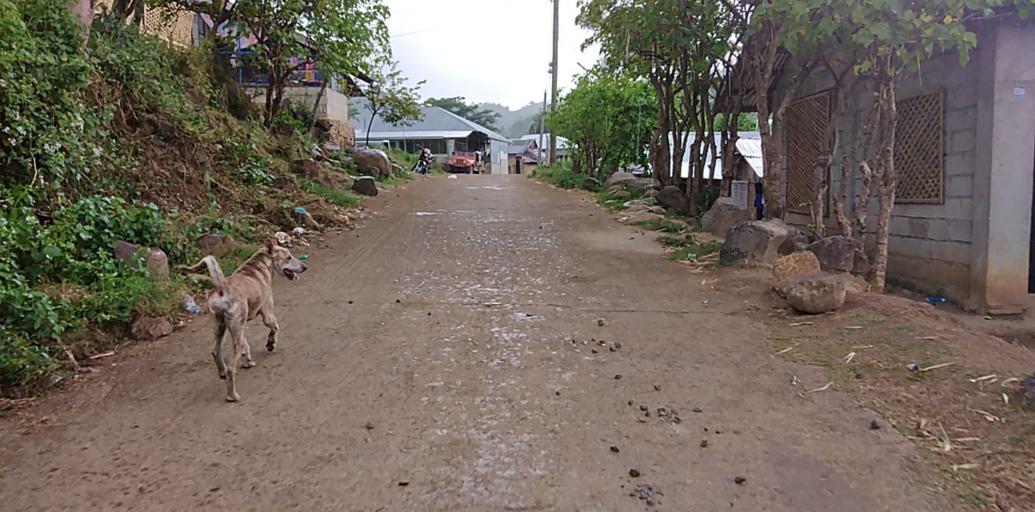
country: PH
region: Central Luzon
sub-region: Province of Pampanga
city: Babo-Pangulo
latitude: 15.1083
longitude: 120.4895
